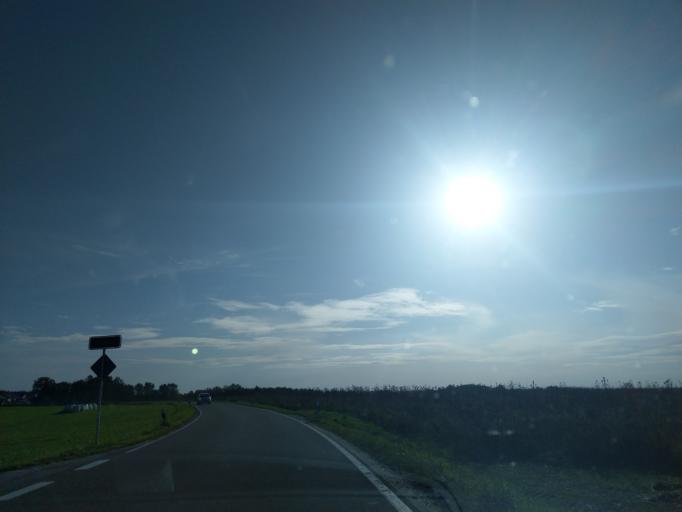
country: DE
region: Bavaria
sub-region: Lower Bavaria
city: Bernried
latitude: 48.8881
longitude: 12.8961
